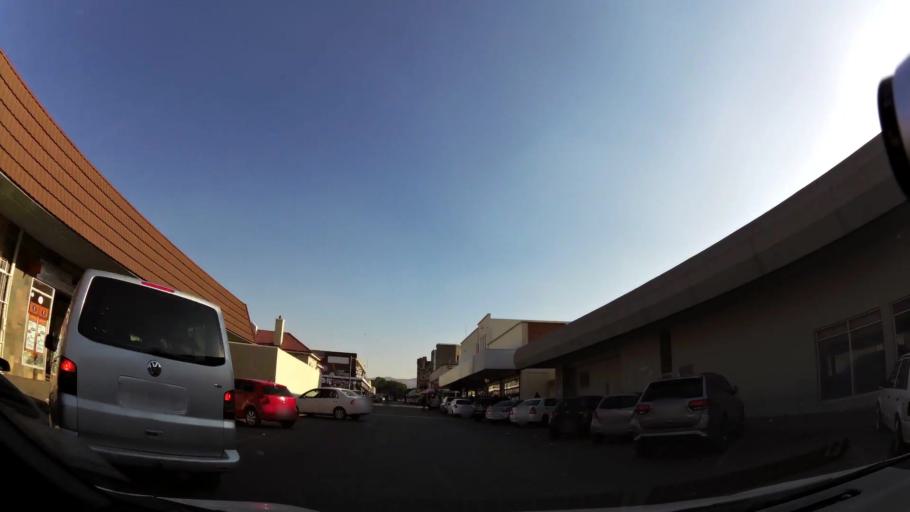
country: ZA
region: North-West
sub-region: Bojanala Platinum District Municipality
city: Rustenburg
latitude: -25.6703
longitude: 27.2447
